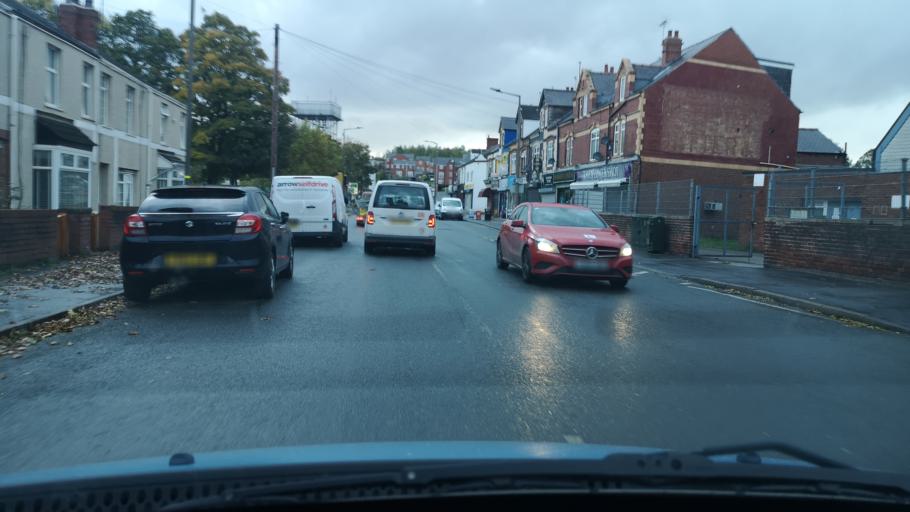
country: GB
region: England
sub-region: Doncaster
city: Askern
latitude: 53.6161
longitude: -1.1493
